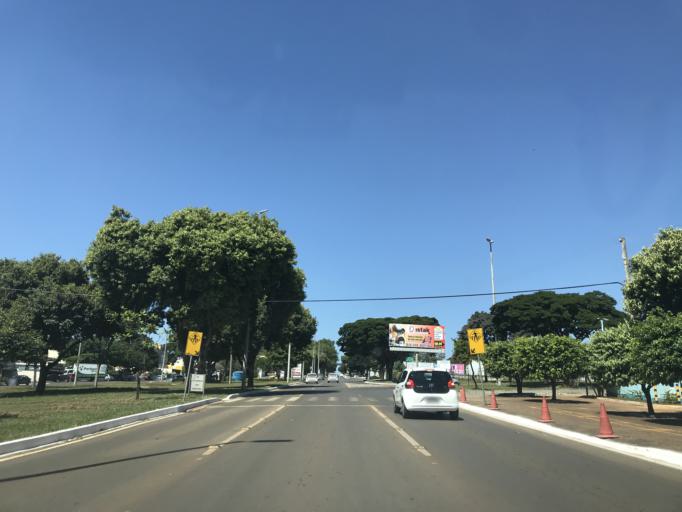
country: BR
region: Federal District
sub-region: Brasilia
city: Brasilia
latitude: -15.6454
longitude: -47.7874
